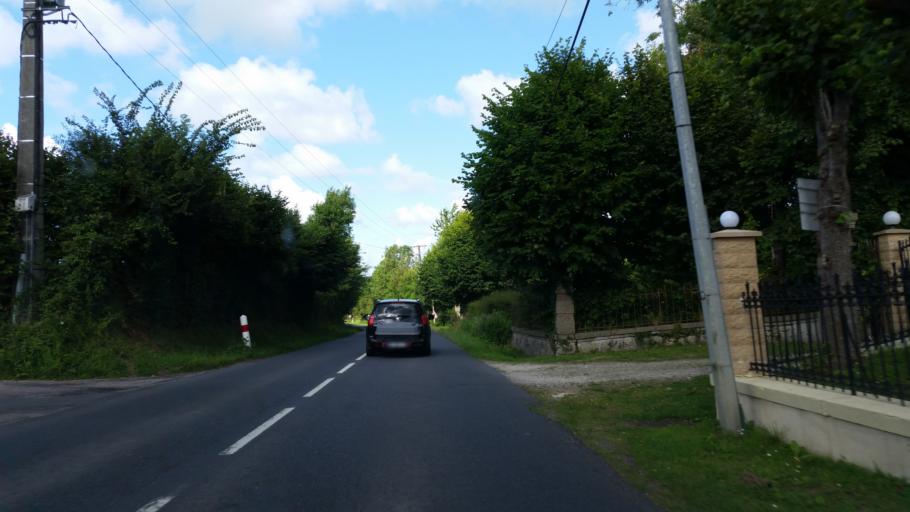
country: FR
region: Lower Normandy
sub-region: Departement du Calvados
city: Blonville-sur-Mer
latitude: 49.3190
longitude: 0.0566
